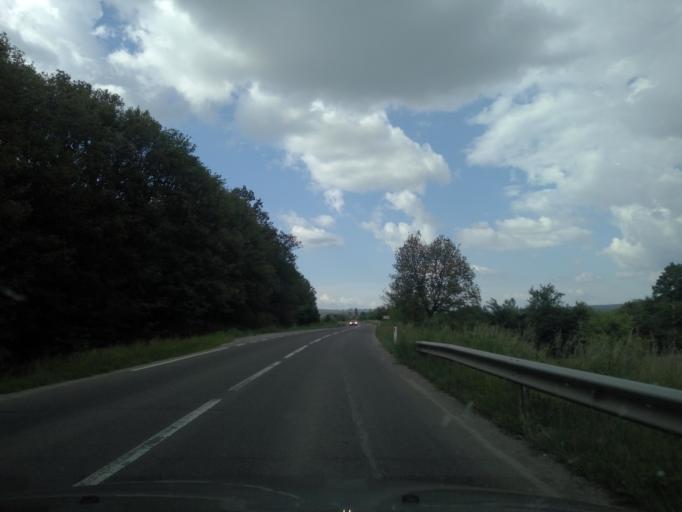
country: XK
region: Gjakova
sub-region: Komuna e Gjakoves
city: Gjakove
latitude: 42.4626
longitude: 20.5049
